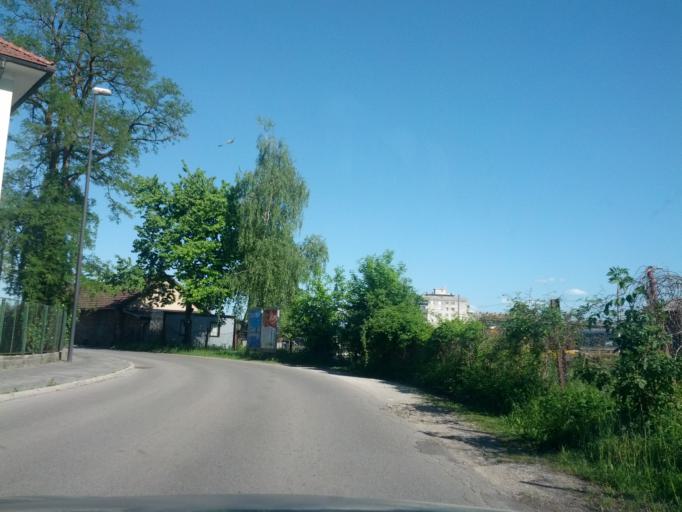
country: SI
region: Ljubljana
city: Ljubljana
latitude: 46.0593
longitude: 14.5223
